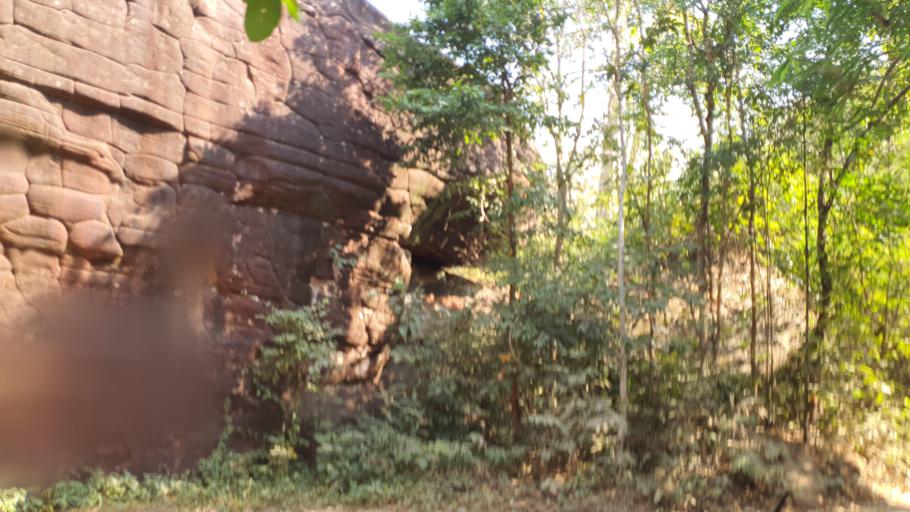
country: TH
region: Changwat Bueng Kan
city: Si Wilai
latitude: 18.2674
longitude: 103.8007
